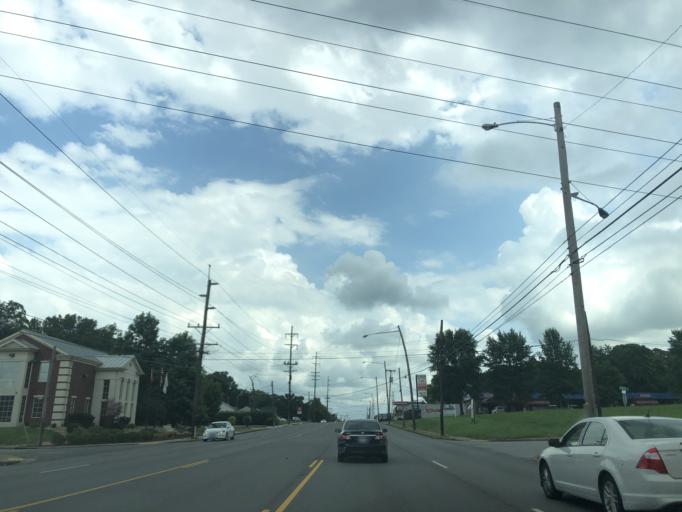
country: US
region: Tennessee
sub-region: Davidson County
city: Lakewood
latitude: 36.1561
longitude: -86.6650
